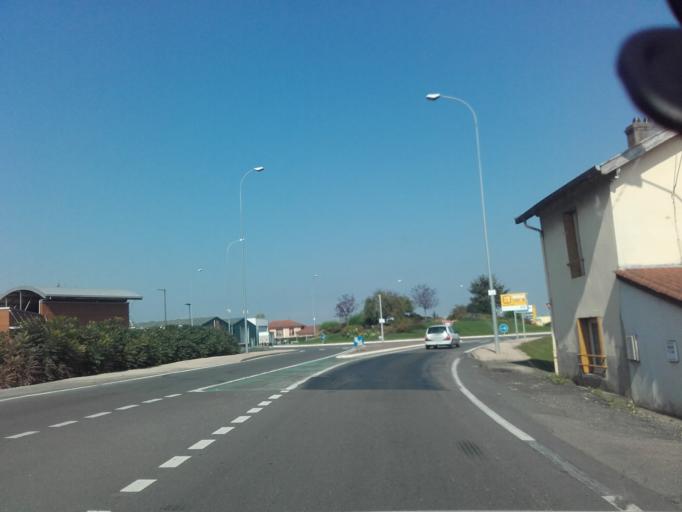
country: FR
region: Bourgogne
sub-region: Departement de Saone-et-Loire
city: Creches-sur-Saone
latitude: 46.2502
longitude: 4.7876
